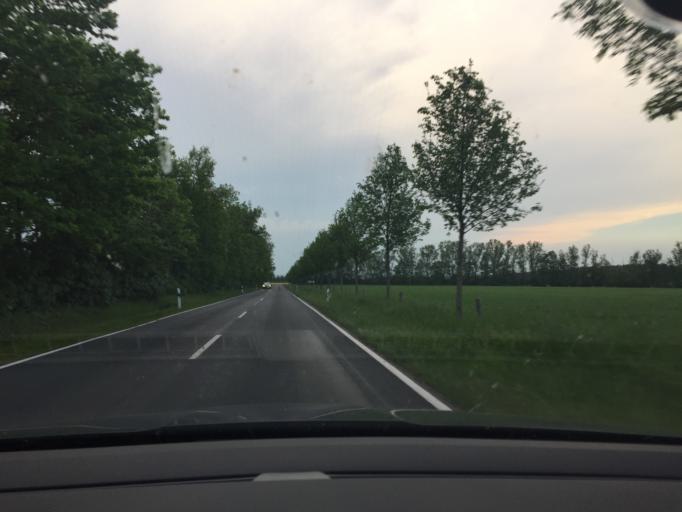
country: DE
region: Brandenburg
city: Niemegk
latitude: 52.0343
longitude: 12.7279
